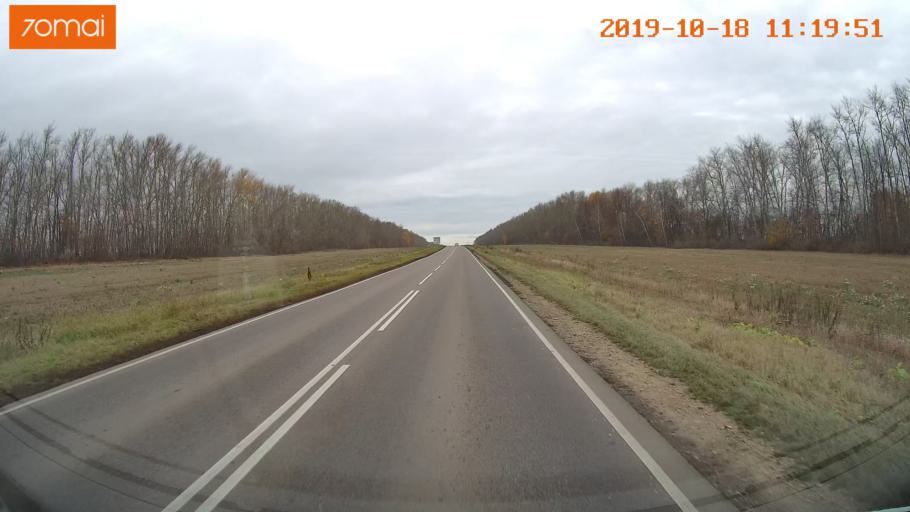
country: RU
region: Tula
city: Kimovsk
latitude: 54.0516
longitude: 38.5558
